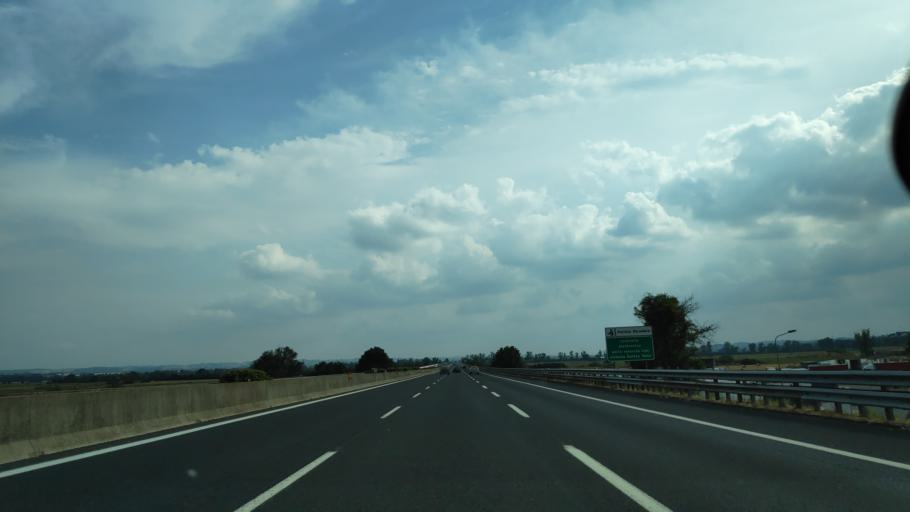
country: IT
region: Latium
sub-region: Citta metropolitana di Roma Capitale
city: Fiano Romano
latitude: 42.1452
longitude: 12.6227
